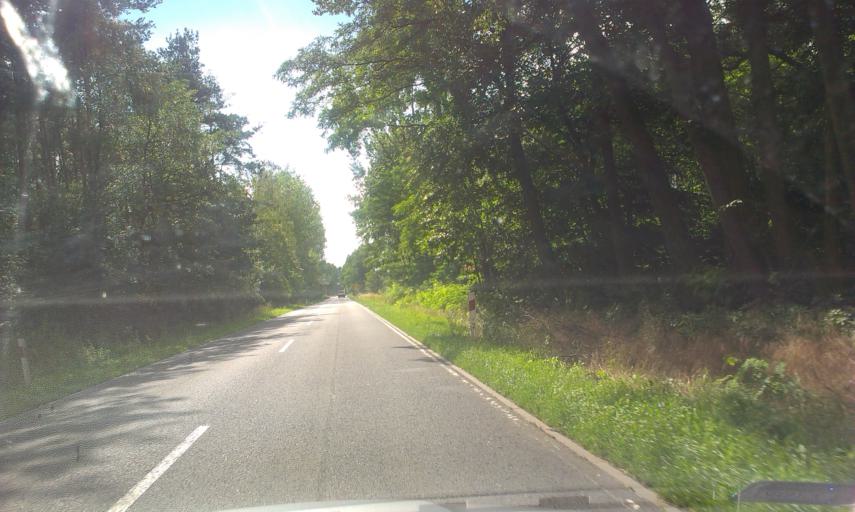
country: PL
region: Lodz Voivodeship
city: Zabia Wola
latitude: 51.9661
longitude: 20.6809
